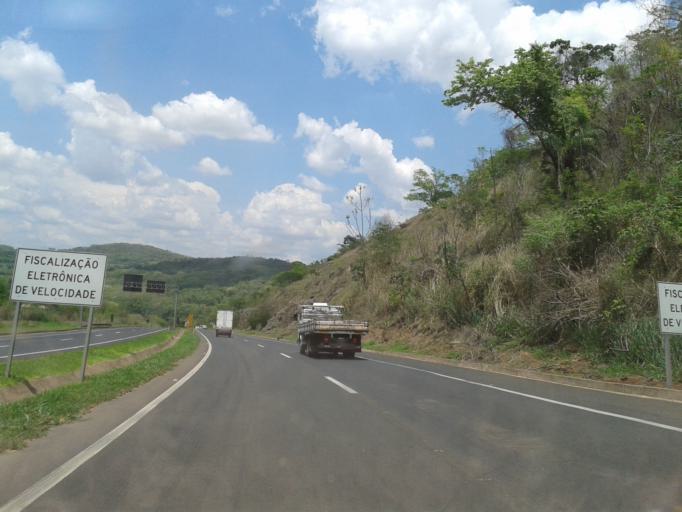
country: BR
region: Minas Gerais
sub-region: Araguari
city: Araguari
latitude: -18.7648
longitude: -48.2440
